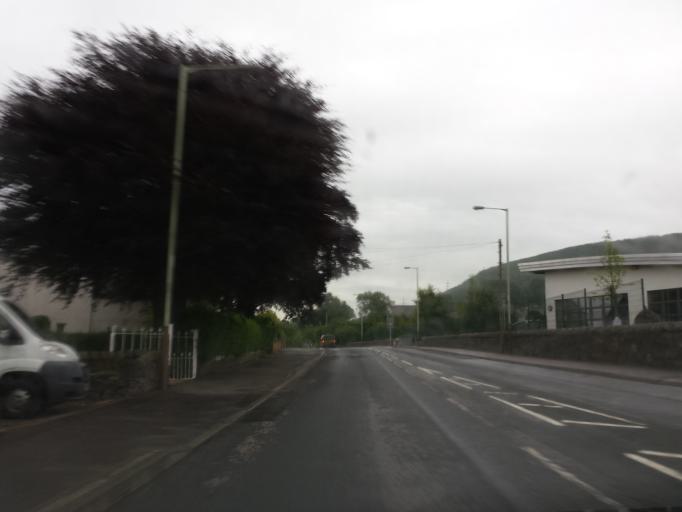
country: GB
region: Scotland
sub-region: Perth and Kinross
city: Abernethy
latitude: 56.3345
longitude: -3.3087
